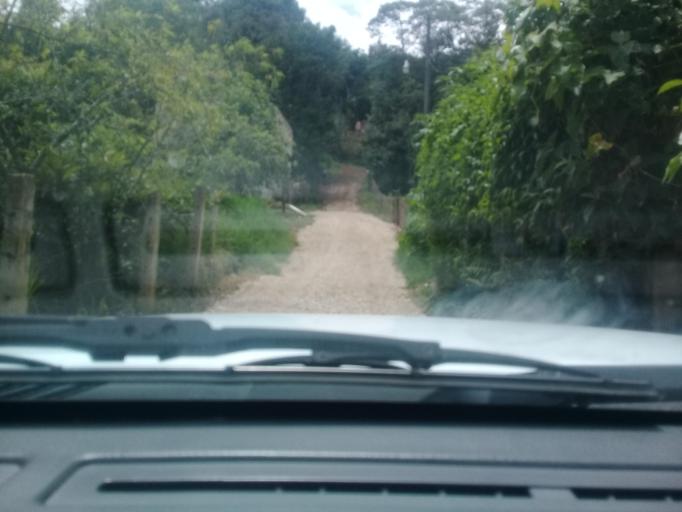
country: MX
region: Veracruz
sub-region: Tlalnelhuayocan
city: Otilpan
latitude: 19.5467
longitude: -96.9778
